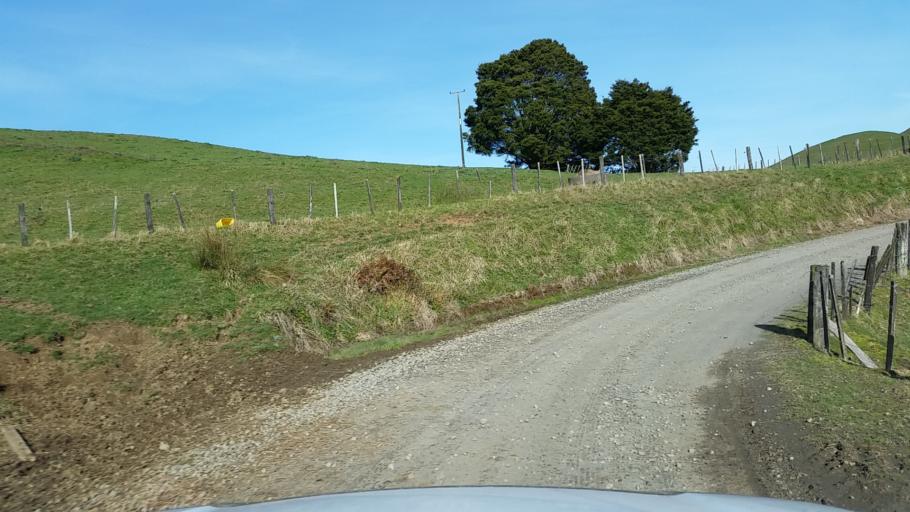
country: NZ
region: Taranaki
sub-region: South Taranaki District
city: Eltham
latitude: -39.3137
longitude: 174.5356
